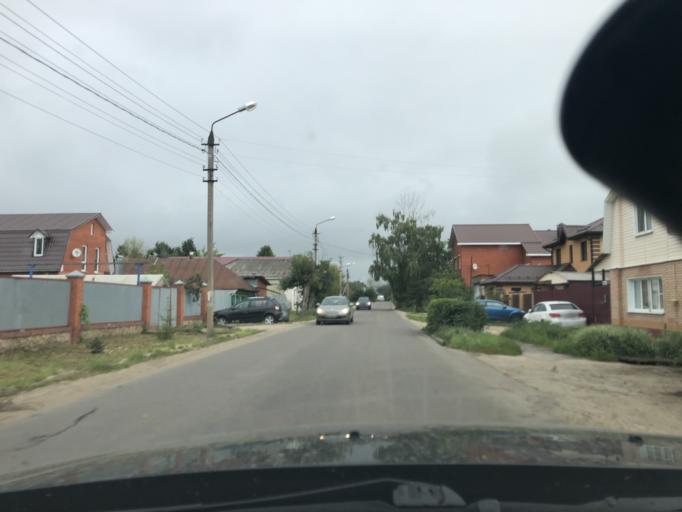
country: RU
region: Tula
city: Tula
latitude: 54.1854
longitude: 37.6345
